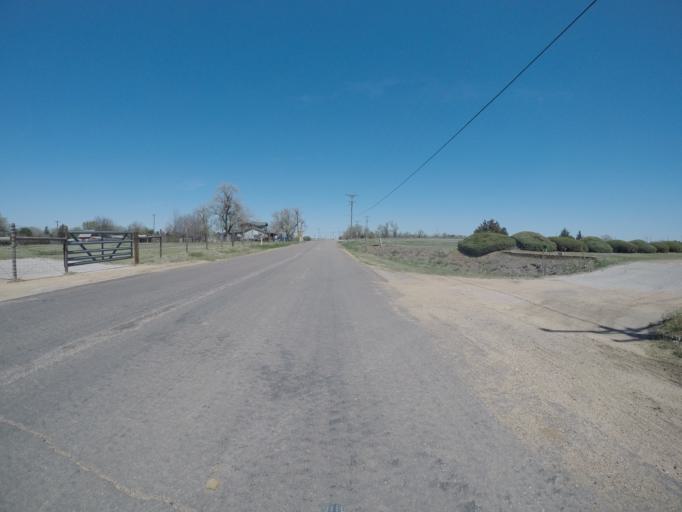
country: US
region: Kansas
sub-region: Pratt County
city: Pratt
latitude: 37.6401
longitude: -98.7668
